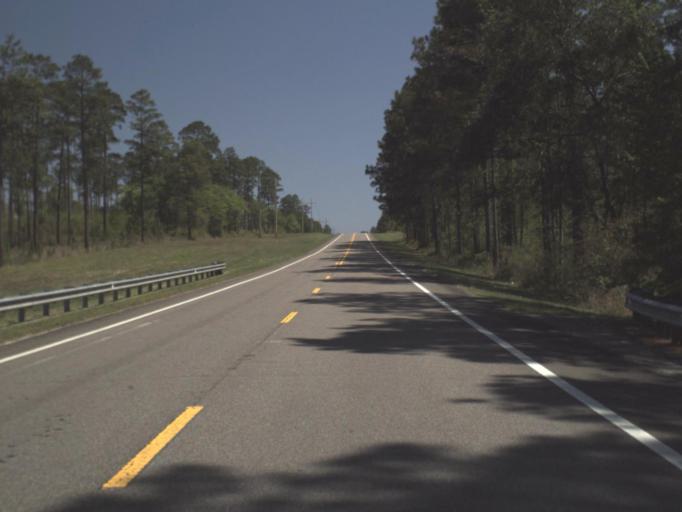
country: US
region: Florida
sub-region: Santa Rosa County
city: Point Baker
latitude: 30.8790
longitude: -86.9509
